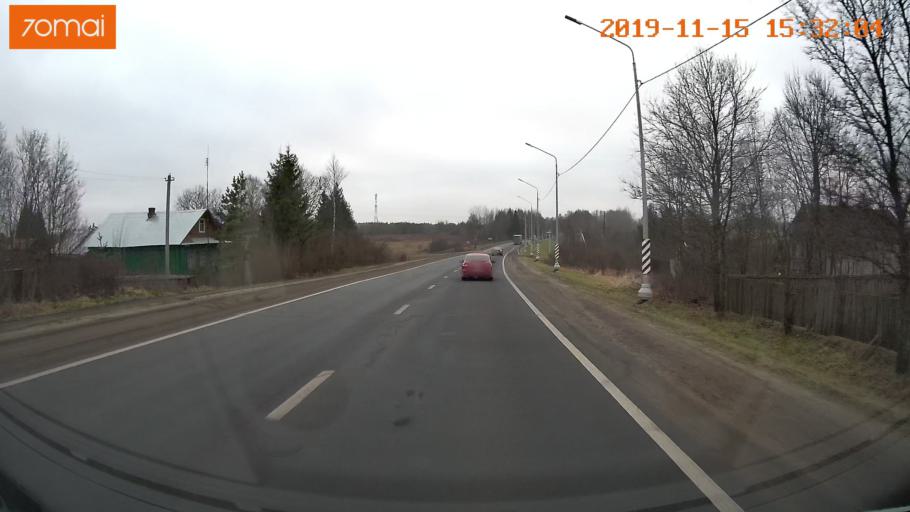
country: RU
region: Jaroslavl
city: Danilov
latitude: 58.0937
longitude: 40.1037
